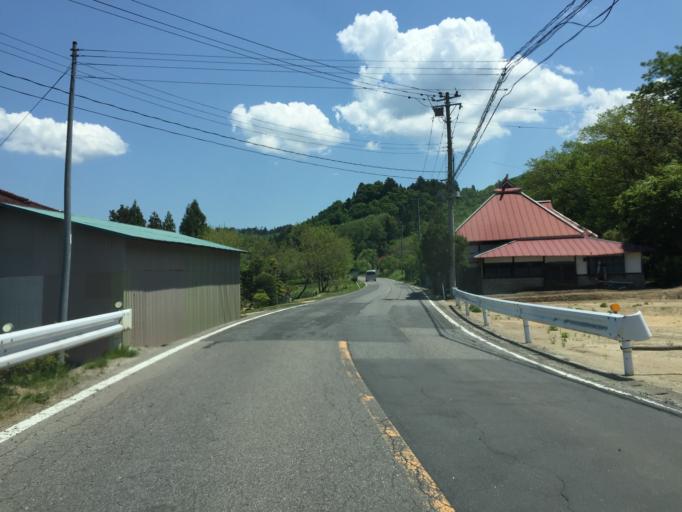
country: JP
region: Fukushima
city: Funehikimachi-funehiki
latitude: 37.4962
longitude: 140.5852
